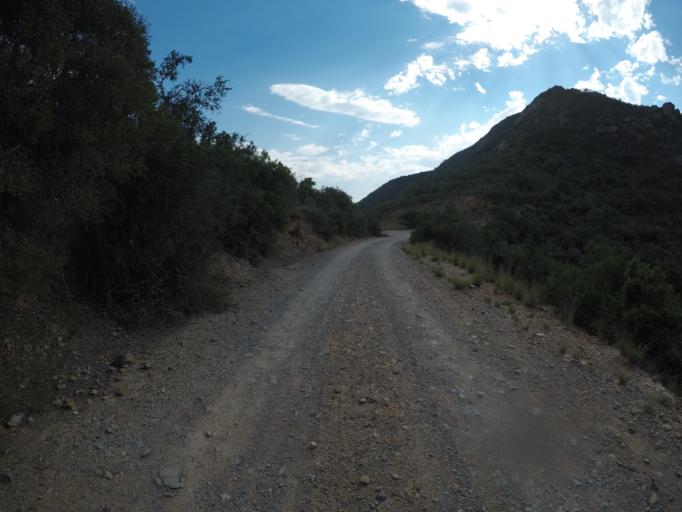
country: ZA
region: Eastern Cape
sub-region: Cacadu District Municipality
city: Kareedouw
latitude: -33.6473
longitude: 24.3399
